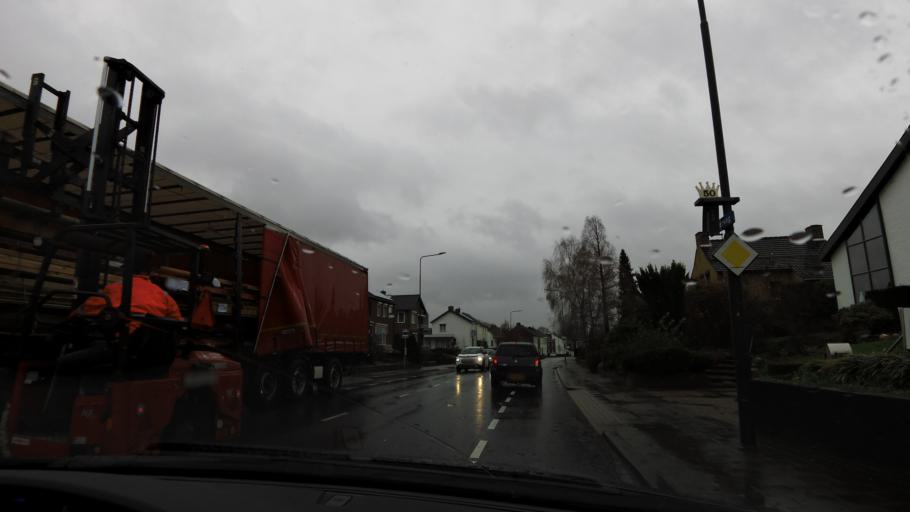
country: NL
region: Limburg
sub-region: Gemeente Sittard-Geleen
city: Limbricht
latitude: 51.0147
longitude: 5.8345
